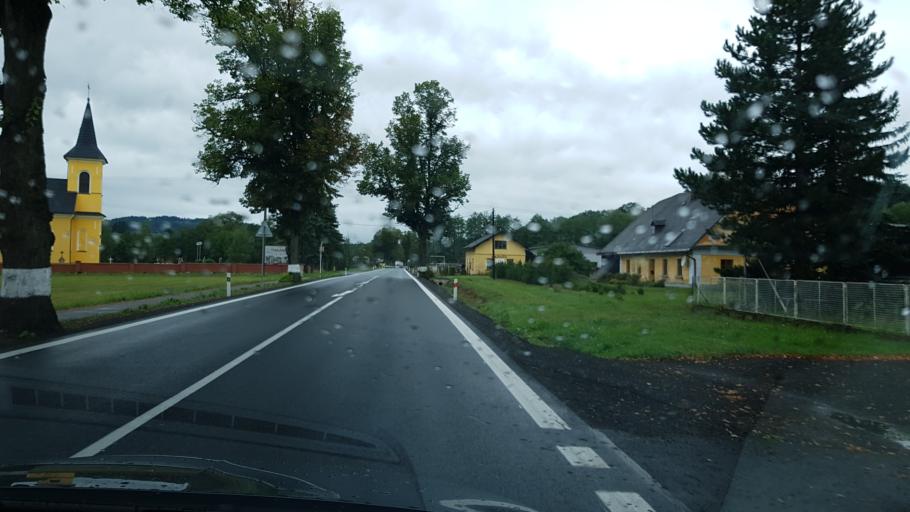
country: CZ
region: Pardubicky
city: Zamberk
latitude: 50.0940
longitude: 16.4416
